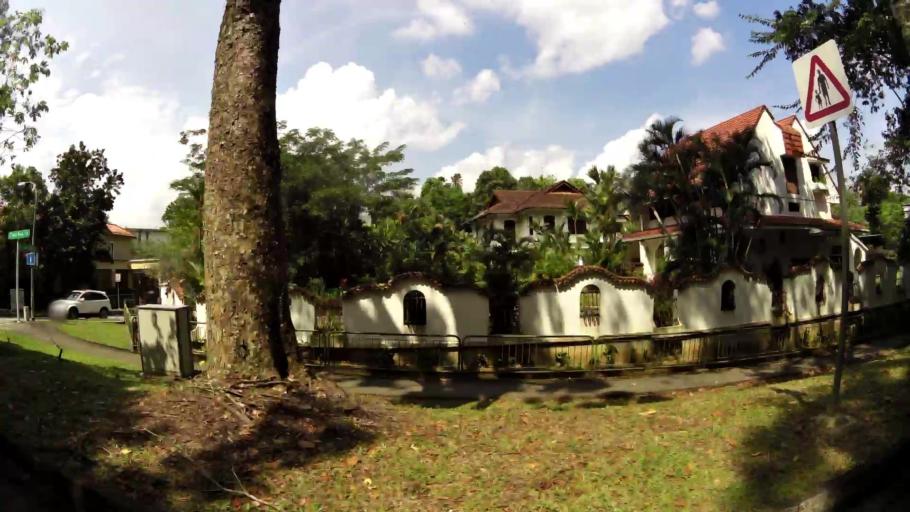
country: SG
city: Singapore
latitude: 1.3167
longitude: 103.8152
